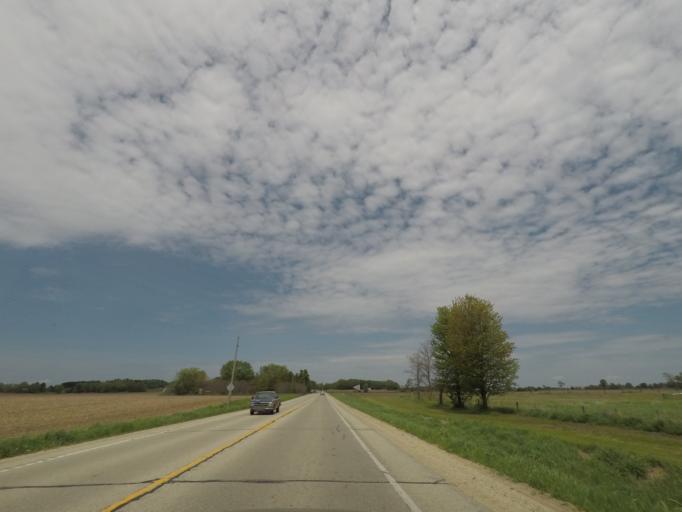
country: US
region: Wisconsin
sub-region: Rock County
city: Evansville
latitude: 42.8115
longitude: -89.2991
